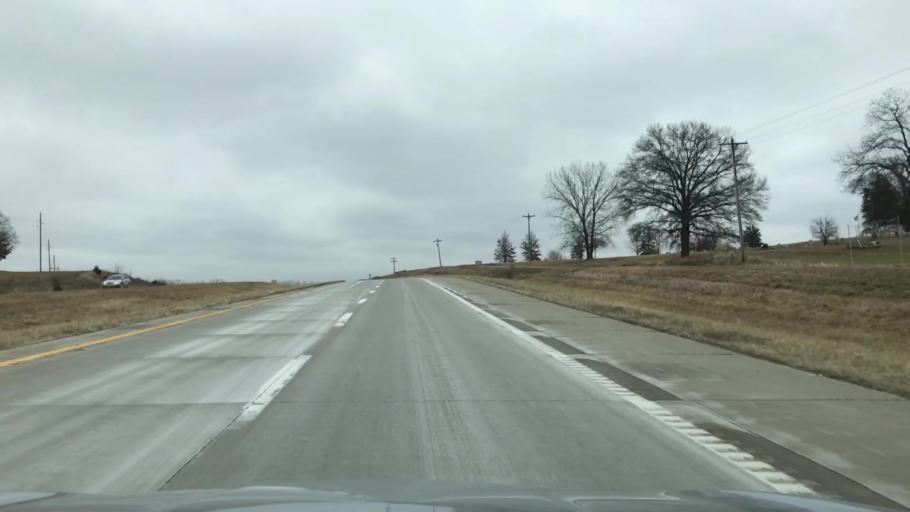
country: US
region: Missouri
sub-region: Livingston County
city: Chillicothe
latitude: 39.7384
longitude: -93.6365
